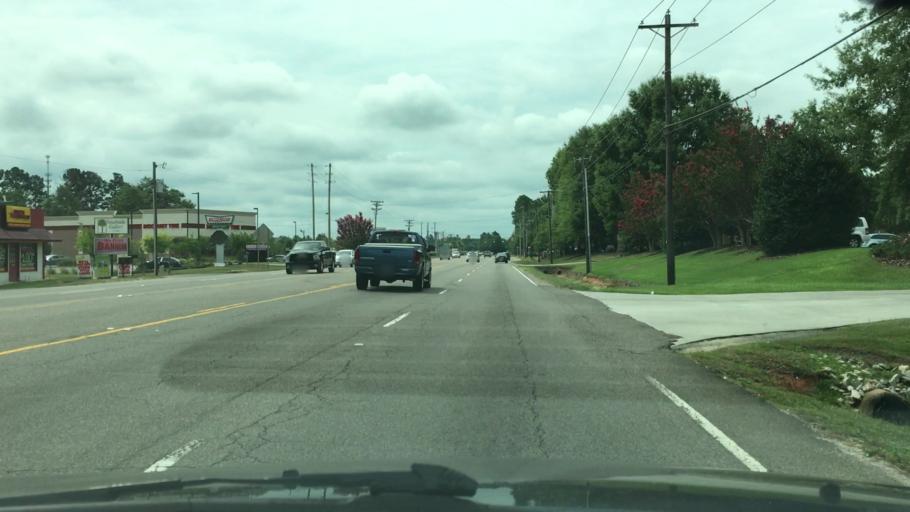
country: US
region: South Carolina
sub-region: Aiken County
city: Aiken
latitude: 33.5137
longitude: -81.7145
